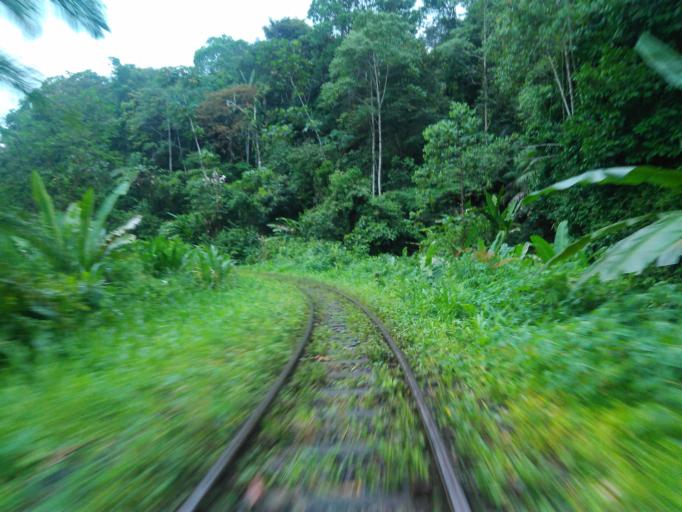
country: CO
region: Valle del Cauca
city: Buenaventura
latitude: 3.8396
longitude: -76.8732
